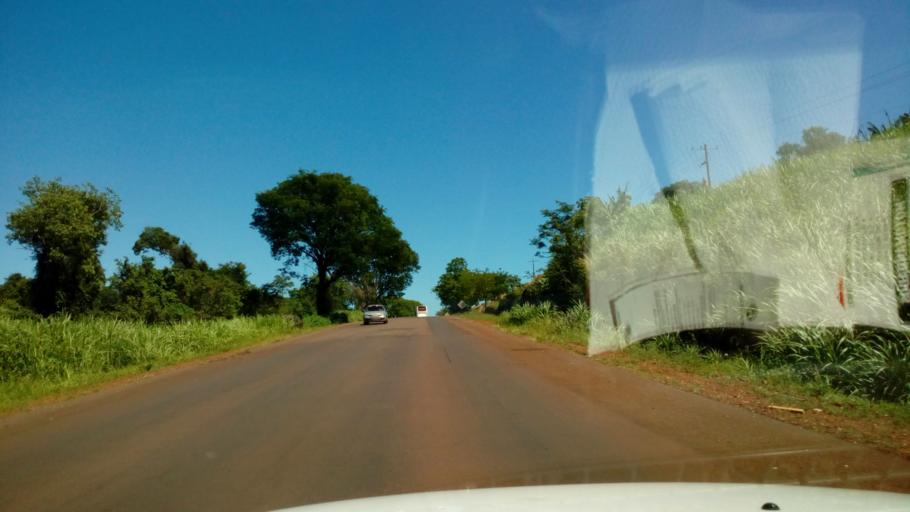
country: AR
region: Misiones
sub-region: Departamento de Leandro N. Alem
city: Leandro N. Alem
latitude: -27.5930
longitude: -55.3560
